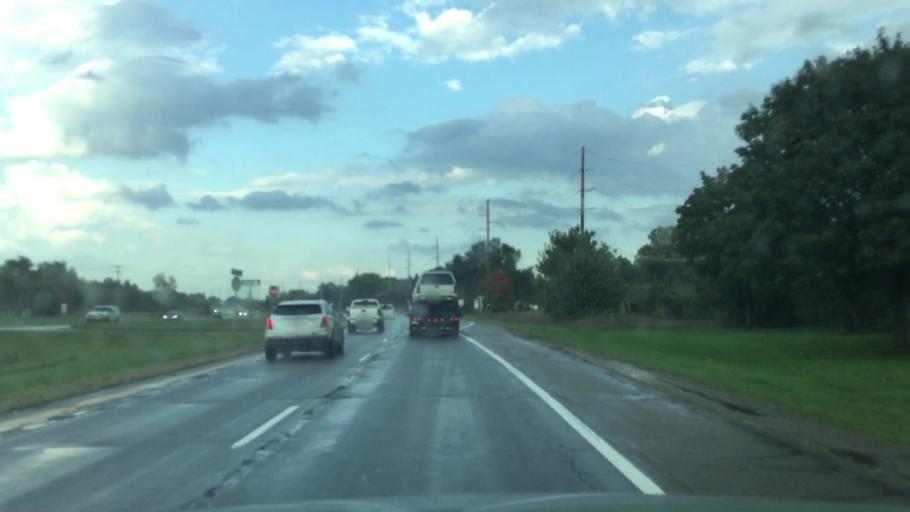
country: US
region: Michigan
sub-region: Oakland County
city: Milford
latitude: 42.6373
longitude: -83.6399
